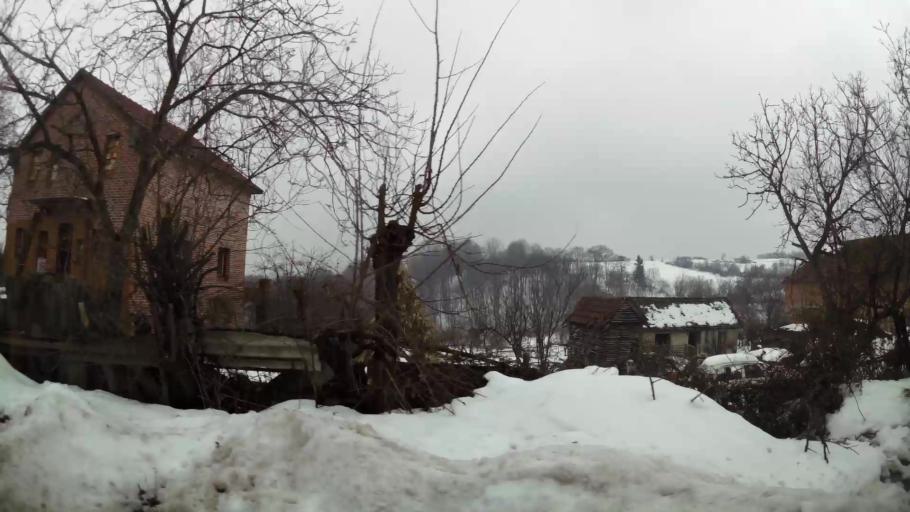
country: RS
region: Central Serbia
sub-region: Belgrade
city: Zvezdara
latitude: 44.7511
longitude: 20.5273
